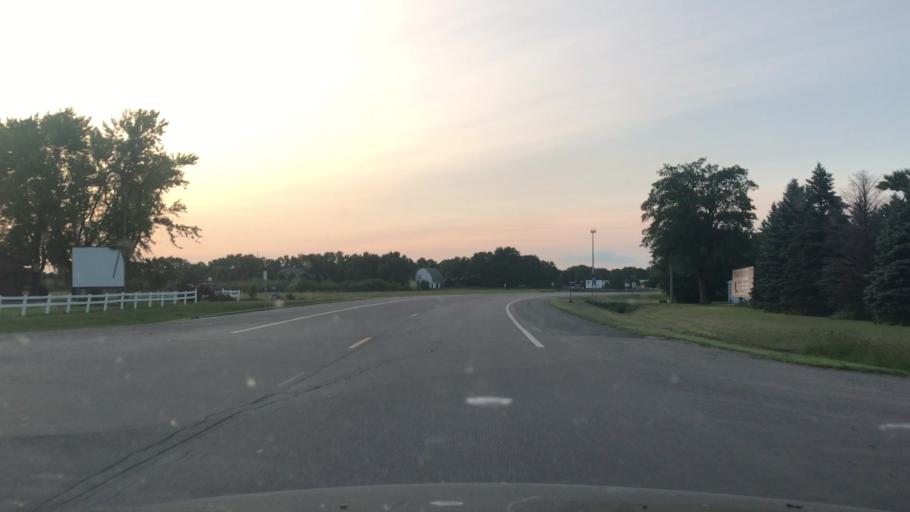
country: US
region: Minnesota
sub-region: Redwood County
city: Redwood Falls
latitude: 44.5252
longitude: -95.1189
